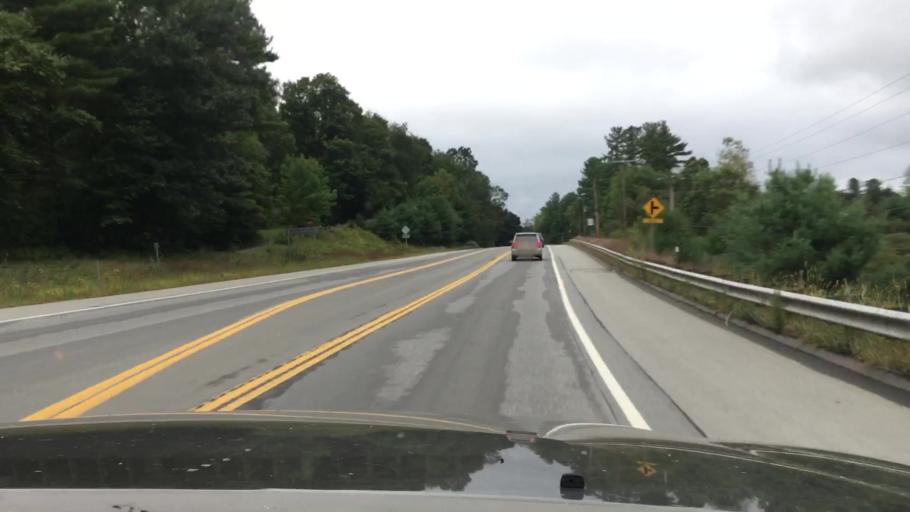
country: US
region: New Hampshire
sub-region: Cheshire County
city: Chesterfield
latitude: 42.8962
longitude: -72.5124
